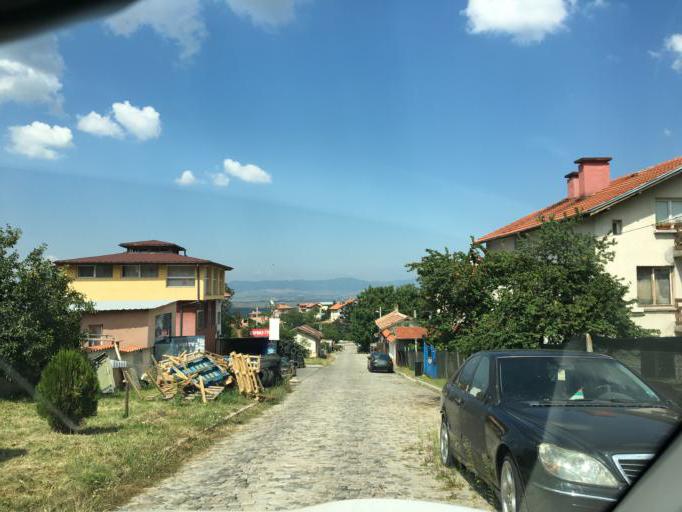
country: BG
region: Sofiya
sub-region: Obshtina Elin Pelin
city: Elin Pelin
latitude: 42.6006
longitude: 23.4778
